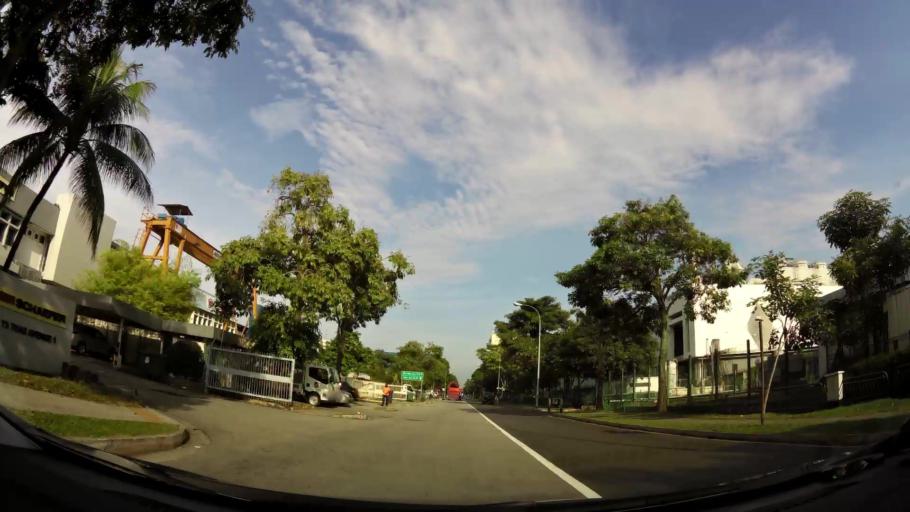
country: MY
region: Johor
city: Johor Bahru
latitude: 1.3301
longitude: 103.6521
